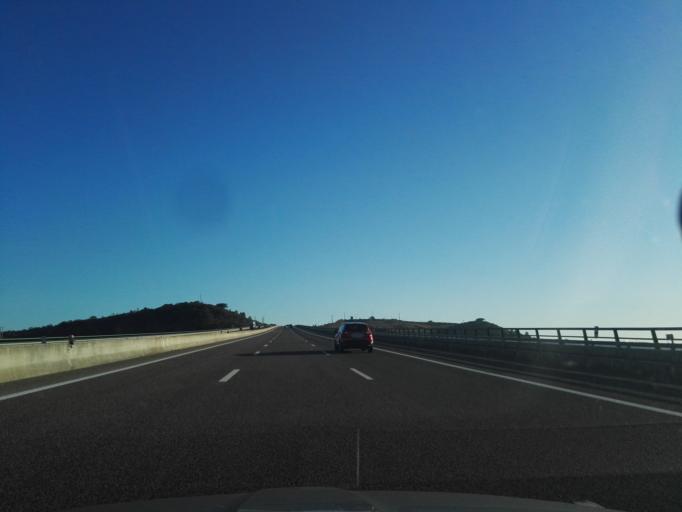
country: PT
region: Lisbon
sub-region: Alenquer
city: Carregado
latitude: 39.0063
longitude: -9.0102
